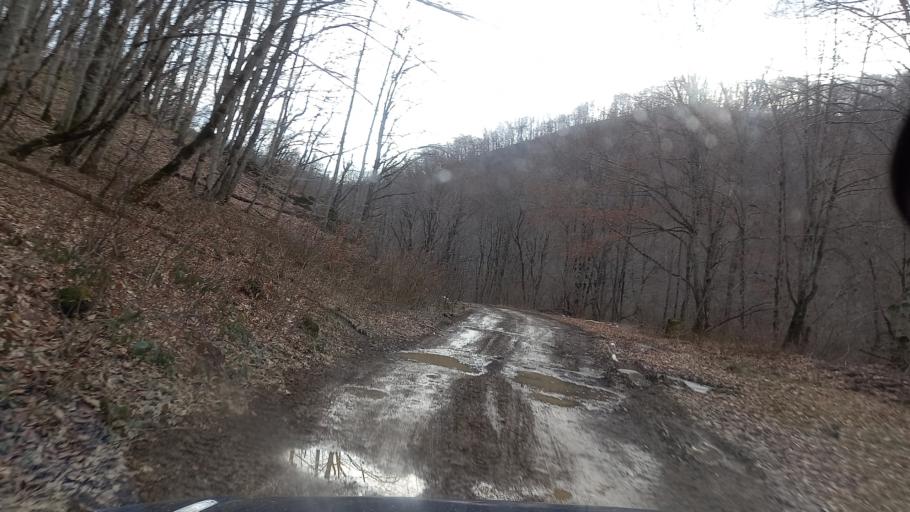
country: RU
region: Adygeya
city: Kamennomostskiy
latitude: 44.1609
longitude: 40.2979
